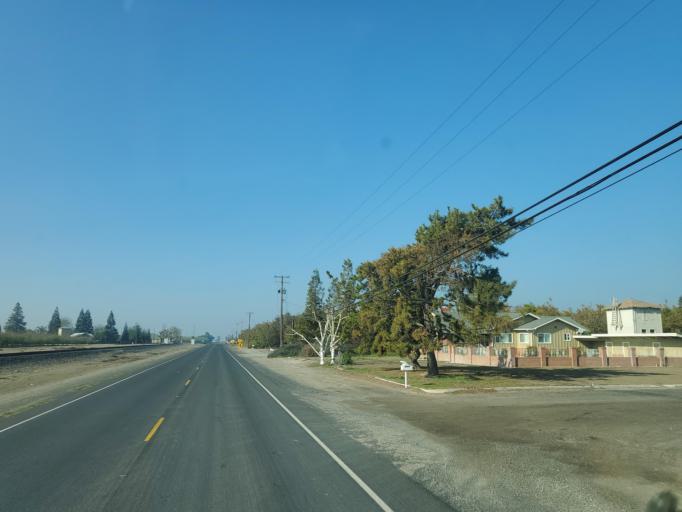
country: US
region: California
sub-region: San Joaquin County
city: Manteca
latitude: 37.8462
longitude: -121.1830
